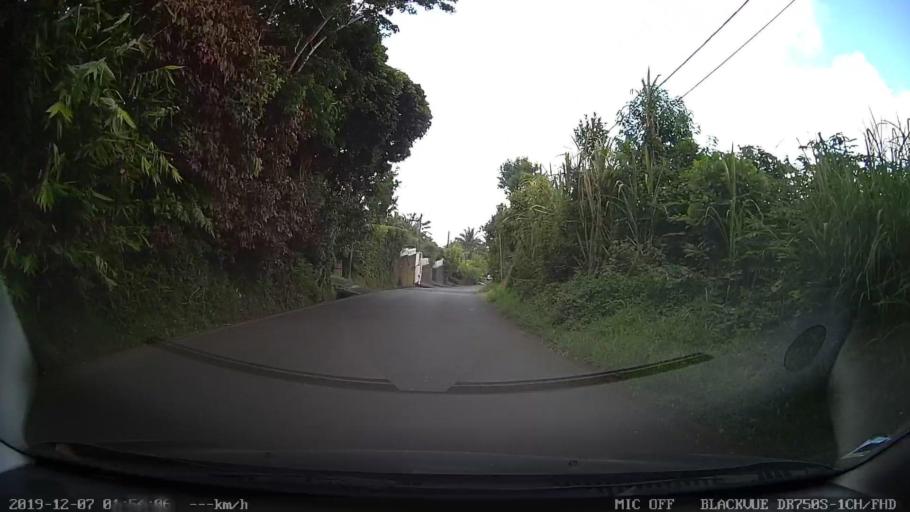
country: RE
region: Reunion
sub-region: Reunion
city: Sainte-Marie
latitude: -20.9355
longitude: 55.5336
